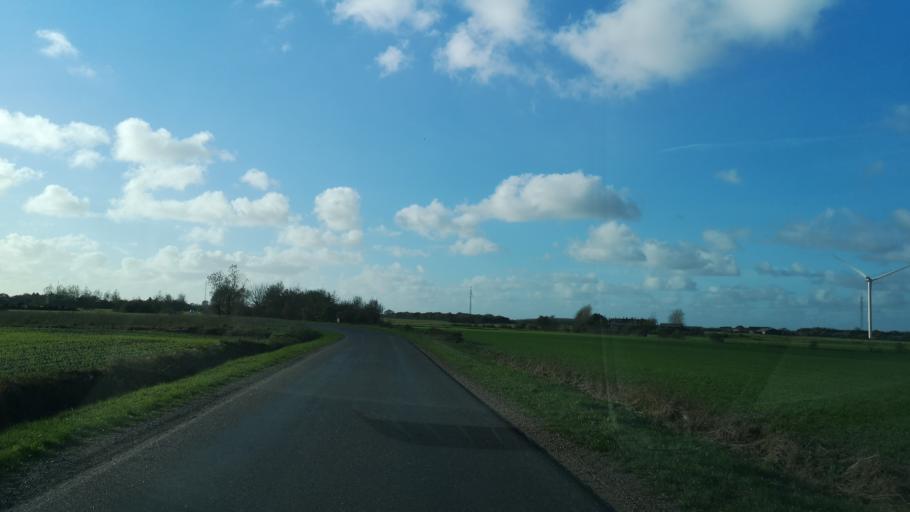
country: DK
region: Central Jutland
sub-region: Ringkobing-Skjern Kommune
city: Skjern
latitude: 55.8381
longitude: 8.3448
